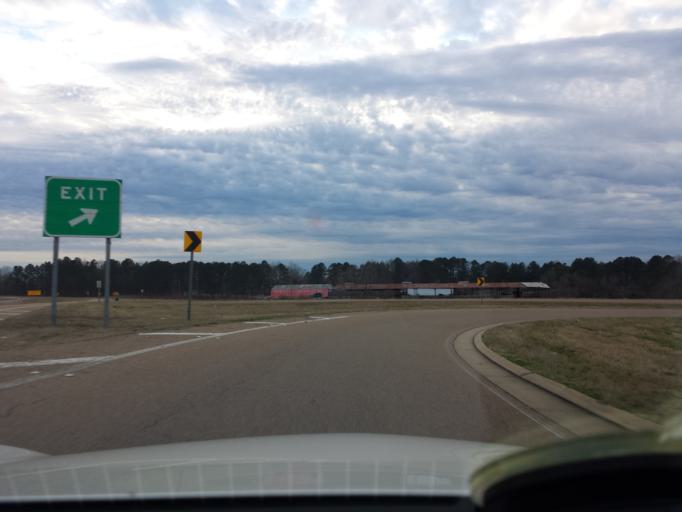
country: US
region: Mississippi
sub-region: Winston County
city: Louisville
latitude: 33.1566
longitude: -89.0881
